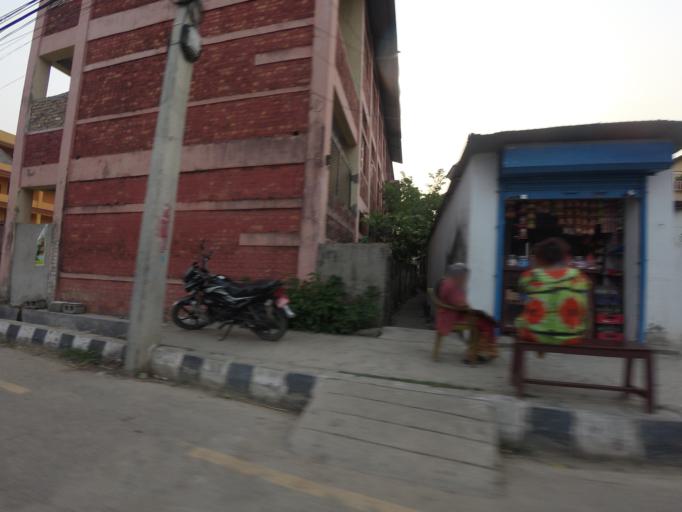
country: NP
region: Western Region
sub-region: Lumbini Zone
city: Bhairahawa
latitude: 27.5039
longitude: 83.4613
